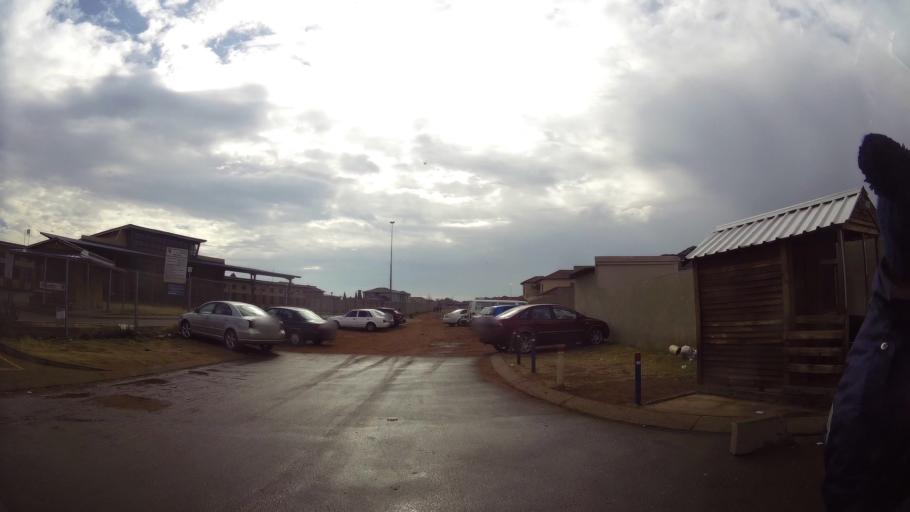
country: ZA
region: Gauteng
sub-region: Ekurhuleni Metropolitan Municipality
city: Germiston
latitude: -26.3268
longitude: 28.1874
